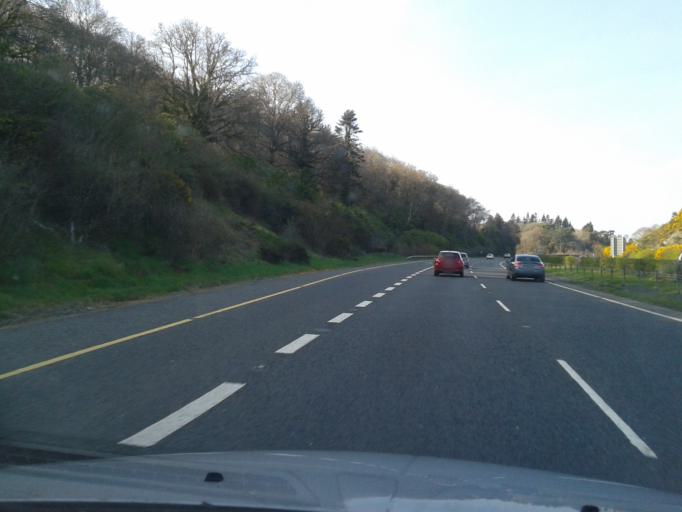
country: IE
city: Newtownmountkennedy
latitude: 53.0579
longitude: -6.0923
